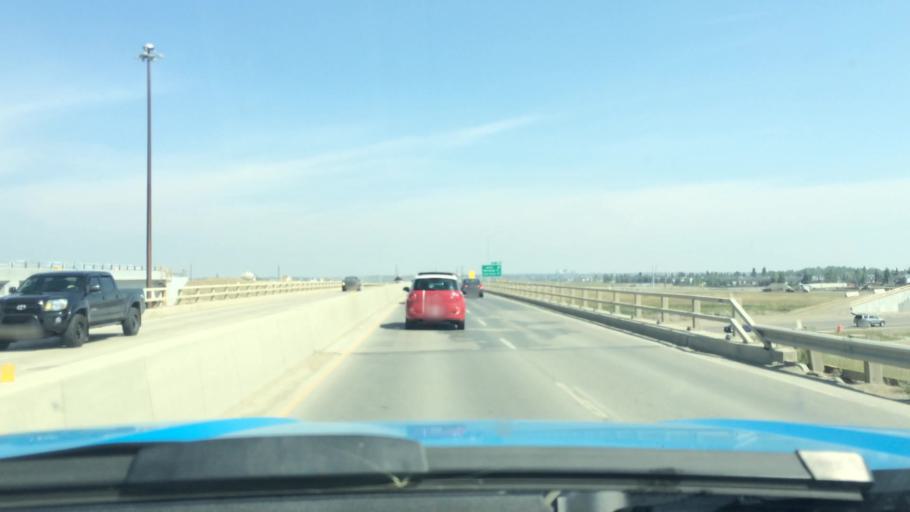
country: CA
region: Alberta
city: Calgary
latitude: 50.8926
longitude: -114.0556
